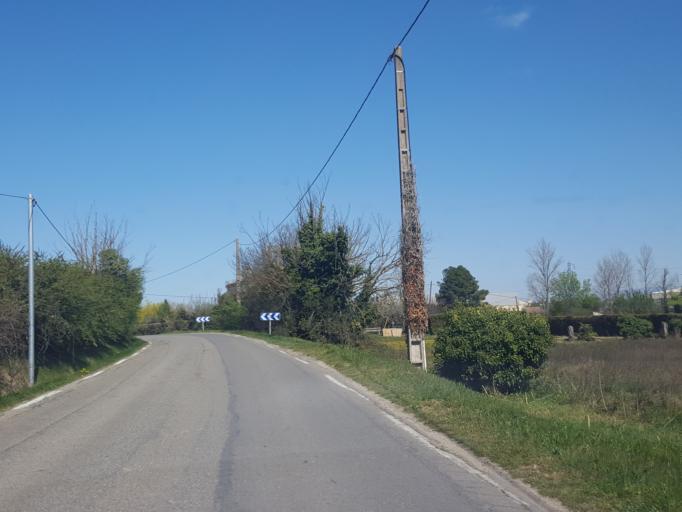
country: FR
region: Provence-Alpes-Cote d'Azur
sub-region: Departement du Vaucluse
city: Entraigues-sur-la-Sorgue
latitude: 43.9887
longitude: 4.9148
